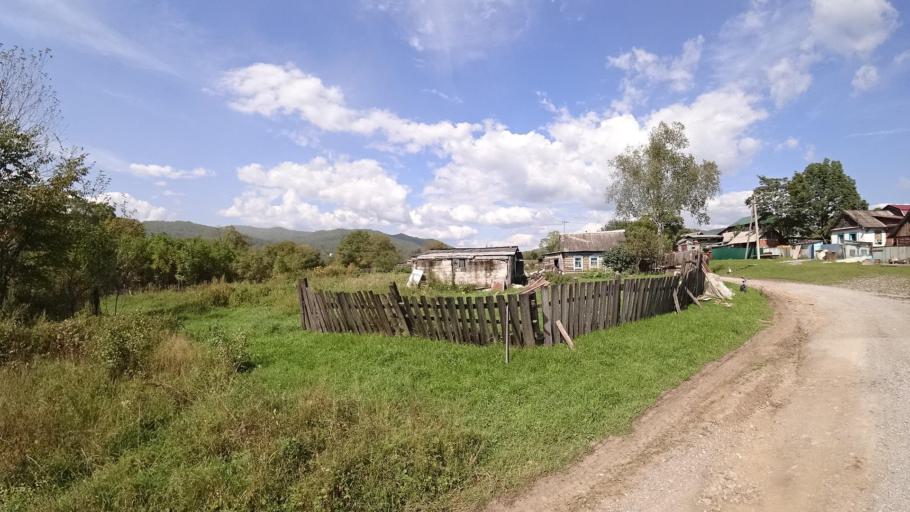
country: RU
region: Jewish Autonomous Oblast
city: Londoko
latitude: 49.0214
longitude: 131.9337
